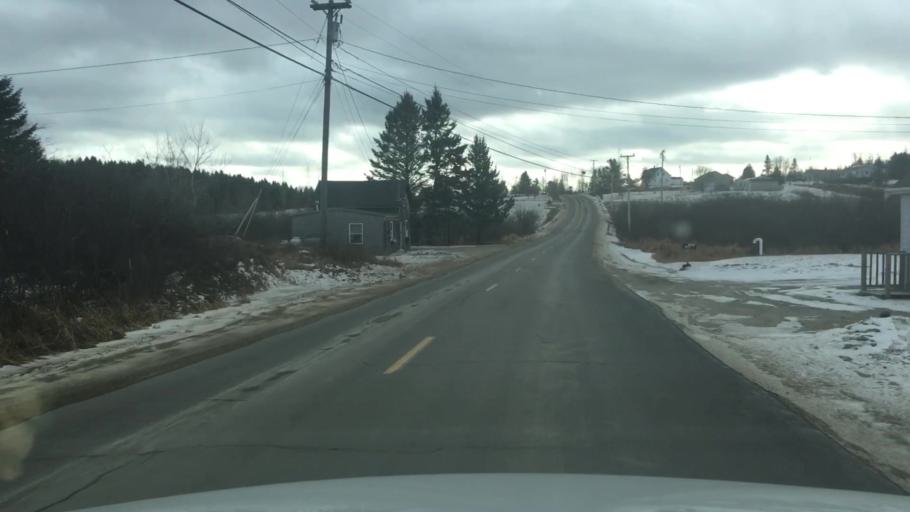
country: US
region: Maine
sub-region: Washington County
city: Machias
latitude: 44.6783
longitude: -67.4674
